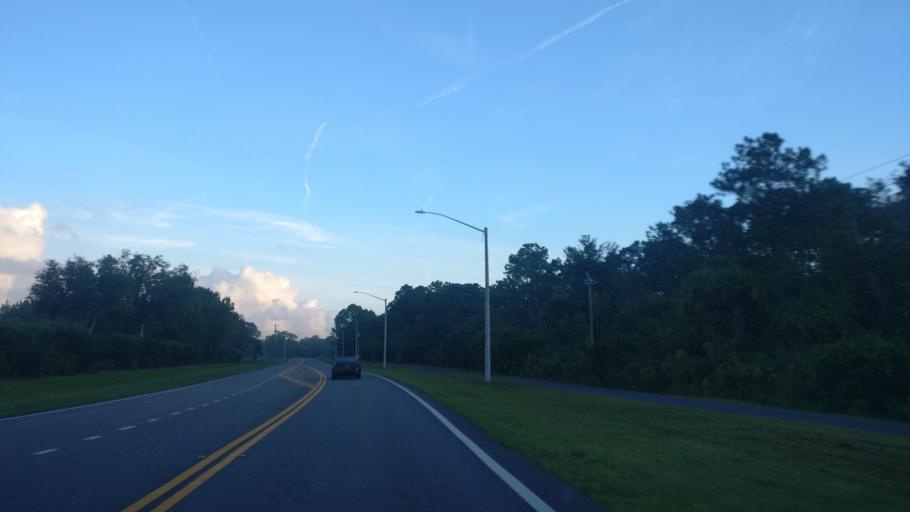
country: US
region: Florida
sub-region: Flagler County
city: Palm Coast
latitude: 29.5305
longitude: -81.2383
